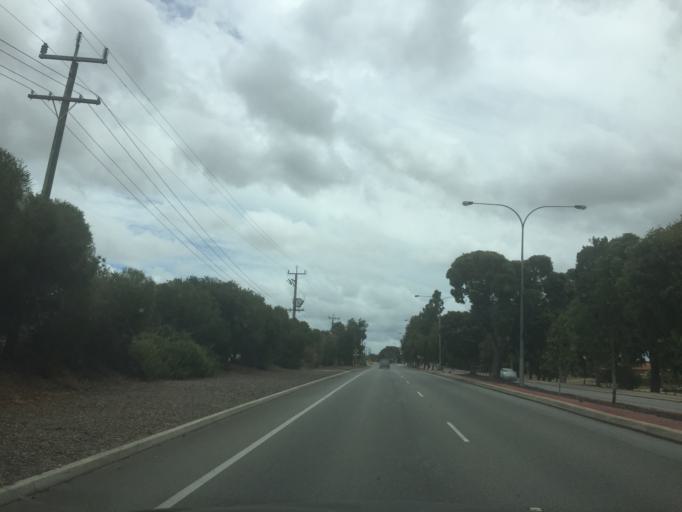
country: AU
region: Western Australia
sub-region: Gosnells
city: Thornlie
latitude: -32.0775
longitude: 115.9461
